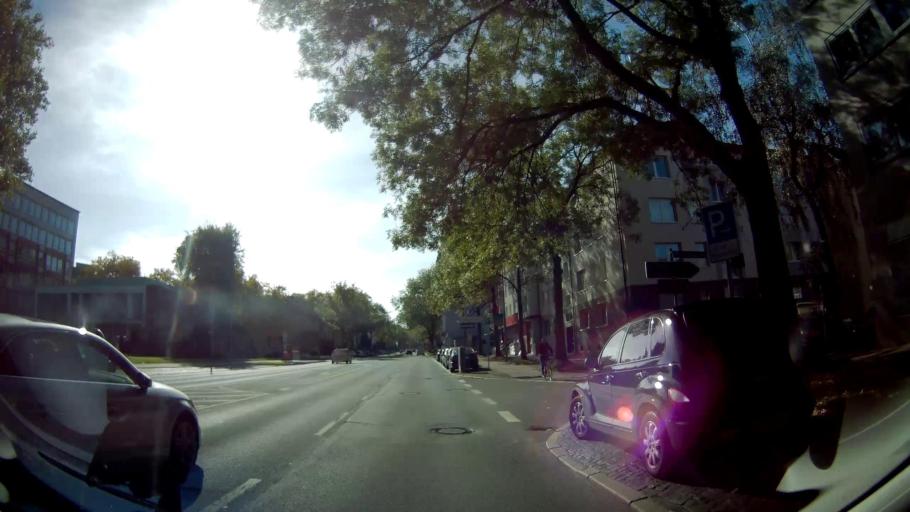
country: DE
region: North Rhine-Westphalia
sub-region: Regierungsbezirk Arnsberg
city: Bochum
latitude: 51.4716
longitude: 7.2169
